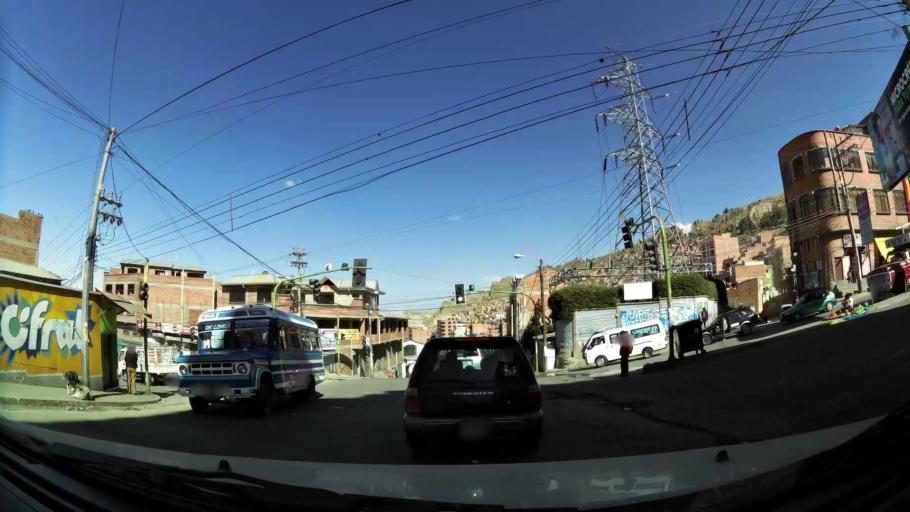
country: BO
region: La Paz
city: La Paz
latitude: -16.5117
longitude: -68.1426
